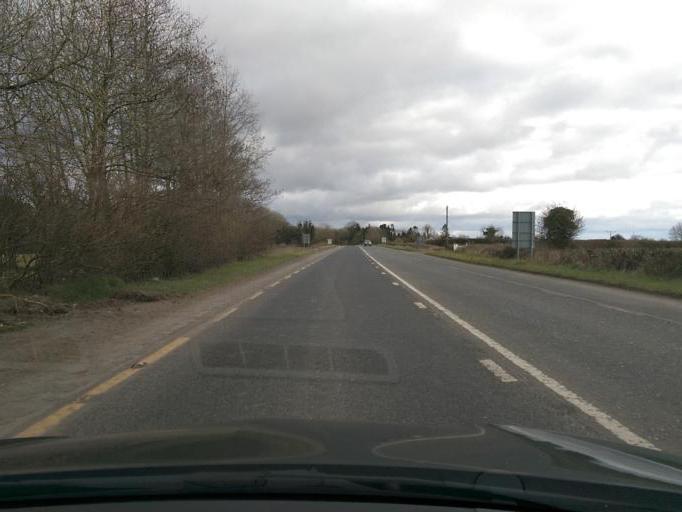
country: IE
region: Leinster
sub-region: An Iarmhi
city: Moate
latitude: 53.3925
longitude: -7.8164
